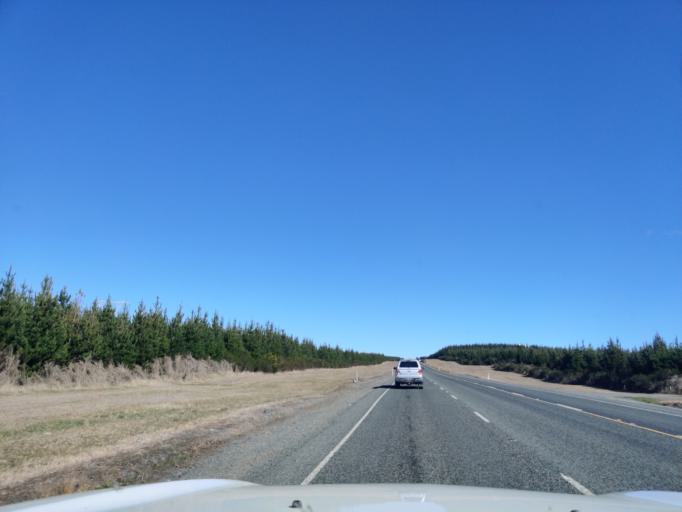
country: NZ
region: Waikato
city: Turangi
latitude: -39.1213
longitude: 175.7985
